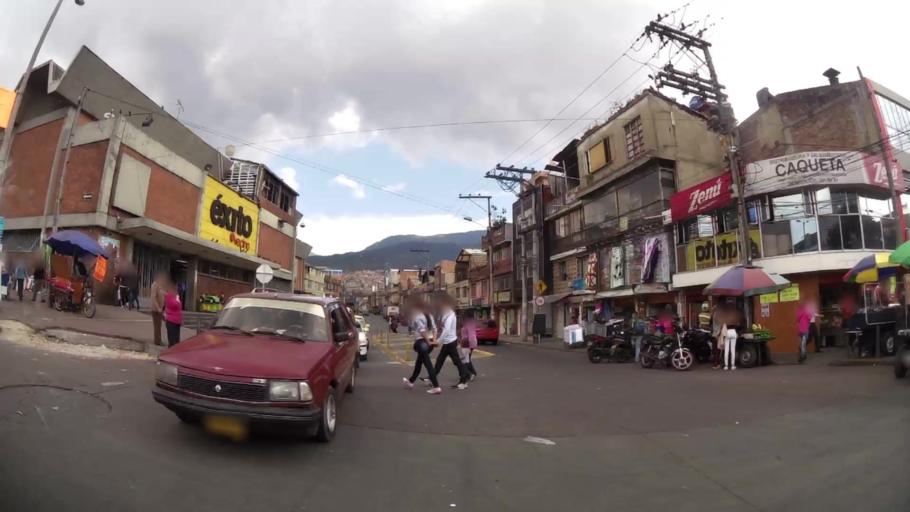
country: CO
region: Bogota D.C.
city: Bogota
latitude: 4.5720
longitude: -74.0921
